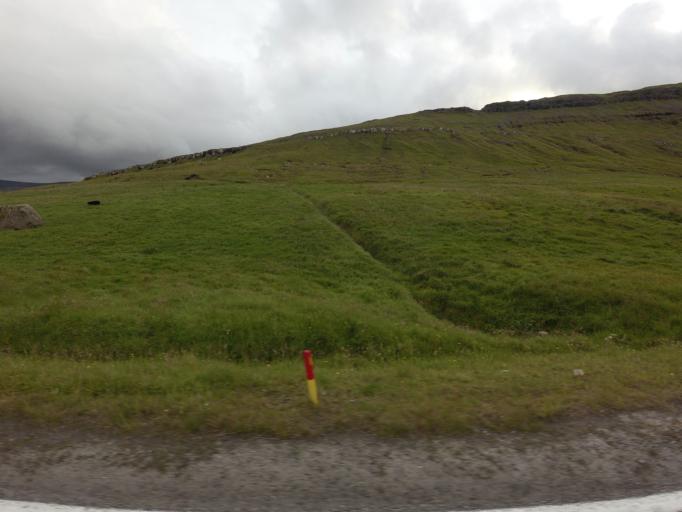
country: FO
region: Streymoy
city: Kollafjordhur
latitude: 62.1303
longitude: -6.8804
